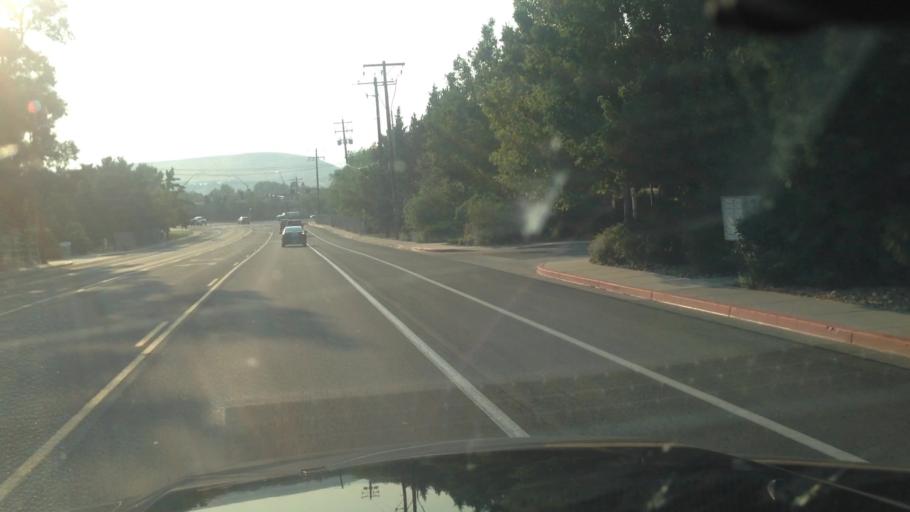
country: US
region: Nevada
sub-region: Washoe County
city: Reno
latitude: 39.5067
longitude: -119.8562
